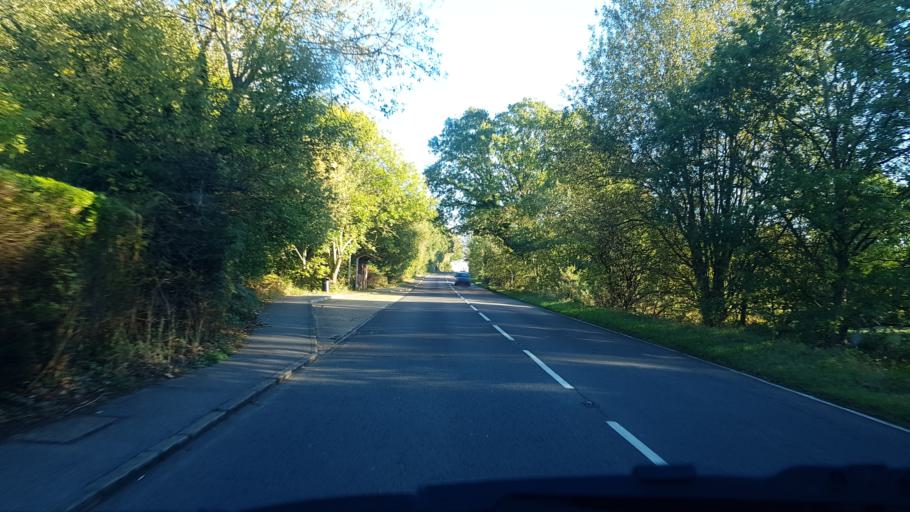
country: GB
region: England
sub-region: Surrey
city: Guildford
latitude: 51.2557
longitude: -0.6070
